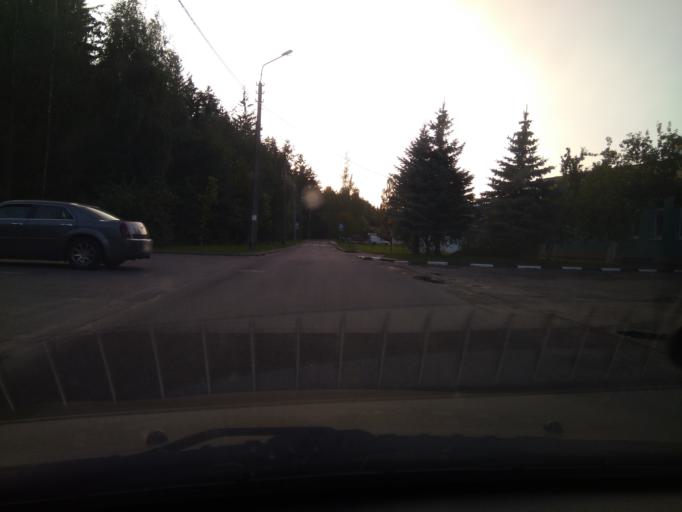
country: BY
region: Minsk
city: Novoye Medvezhino
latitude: 53.8917
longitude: 27.4493
